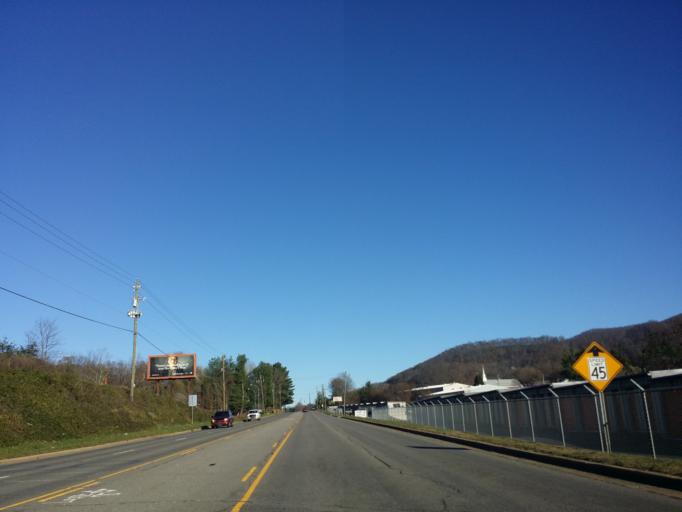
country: US
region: North Carolina
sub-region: Buncombe County
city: Swannanoa
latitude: 35.5932
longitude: -82.4348
